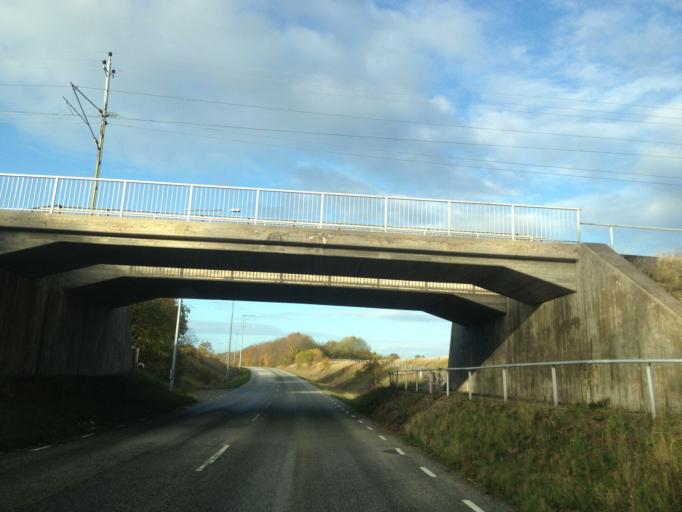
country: SE
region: Skane
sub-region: Lomma Kommun
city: Lomma
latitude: 55.6638
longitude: 13.0750
